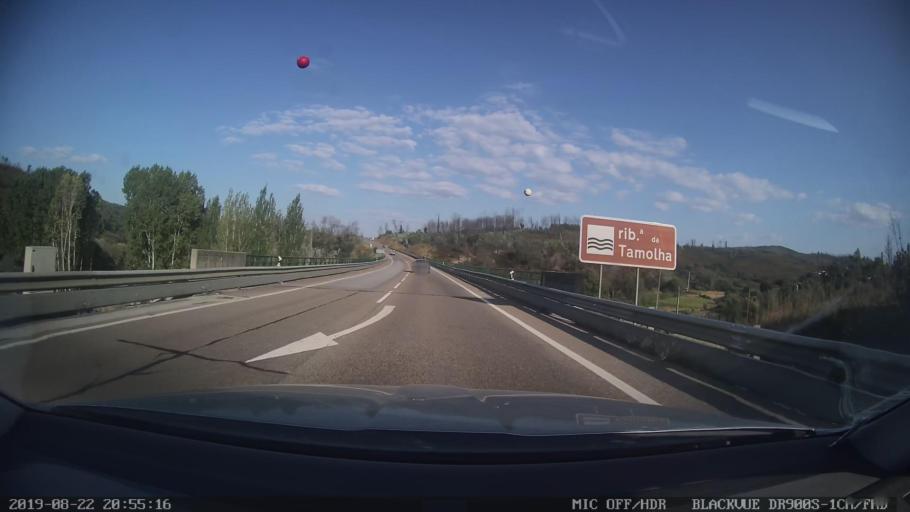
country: PT
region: Castelo Branco
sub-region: Serta
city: Serta
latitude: 39.7791
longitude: -8.0293
